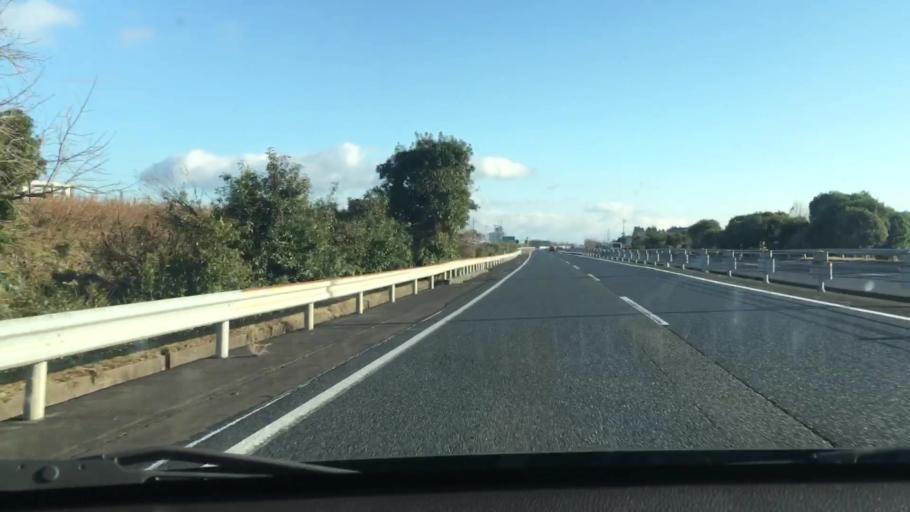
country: JP
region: Kagoshima
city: Kajiki
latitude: 31.8033
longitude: 130.7106
